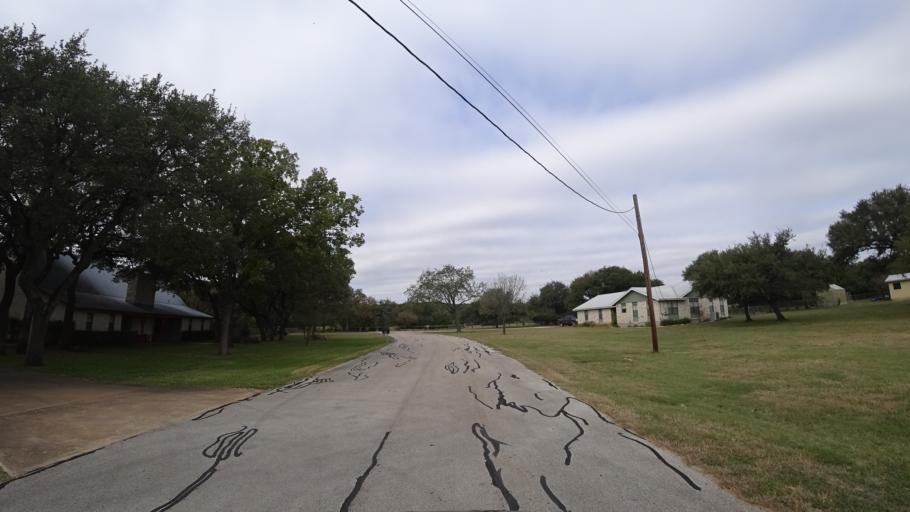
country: US
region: Texas
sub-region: Travis County
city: Shady Hollow
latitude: 30.1362
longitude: -97.8988
